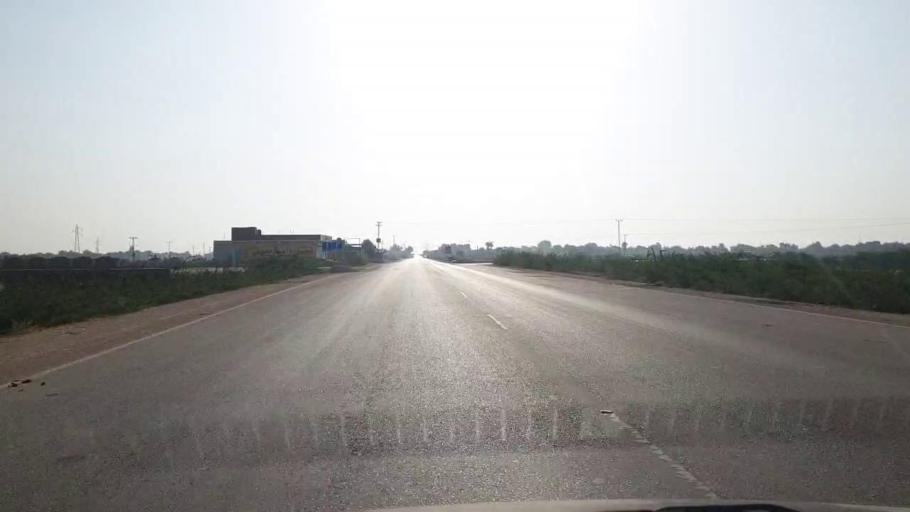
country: PK
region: Sindh
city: Badin
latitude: 24.6784
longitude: 68.8448
